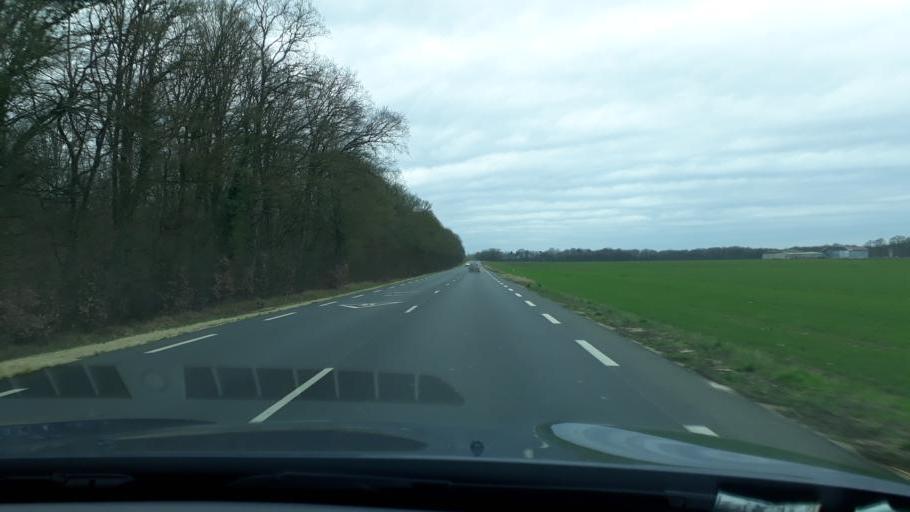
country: FR
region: Centre
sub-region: Departement du Loiret
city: Chanteau
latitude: 48.0215
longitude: 1.9657
